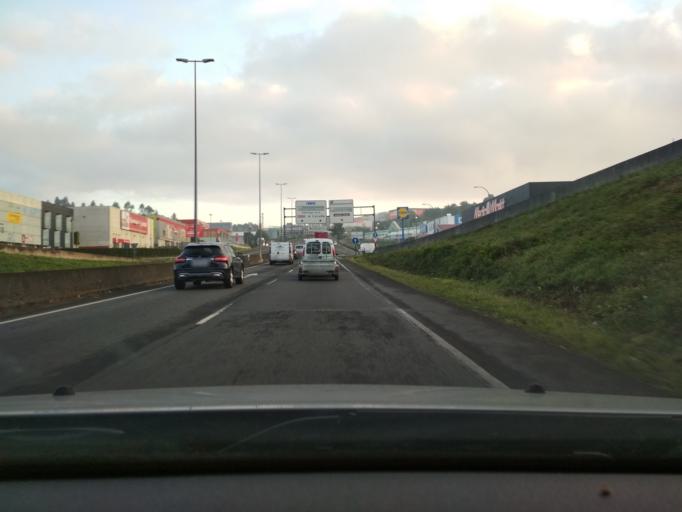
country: ES
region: Galicia
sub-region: Provincia da Coruna
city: Santiago de Compostela
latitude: 42.8992
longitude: -8.5100
